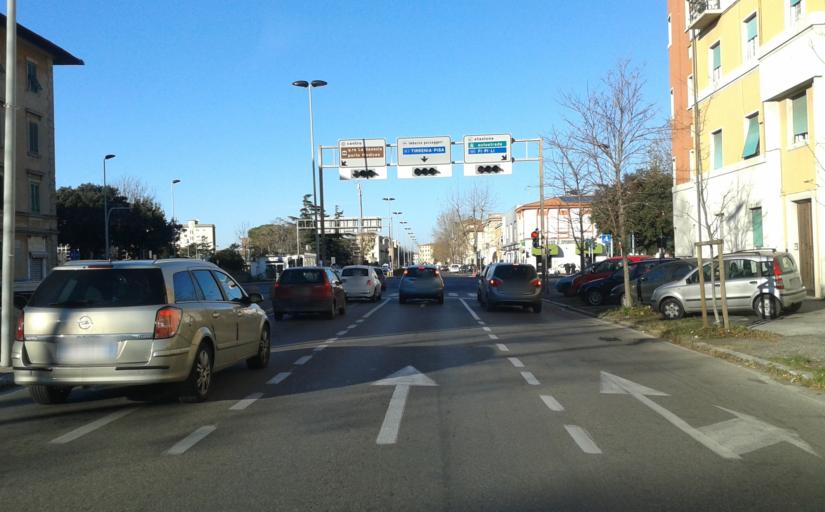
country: IT
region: Tuscany
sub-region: Provincia di Livorno
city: Livorno
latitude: 43.5529
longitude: 10.3273
